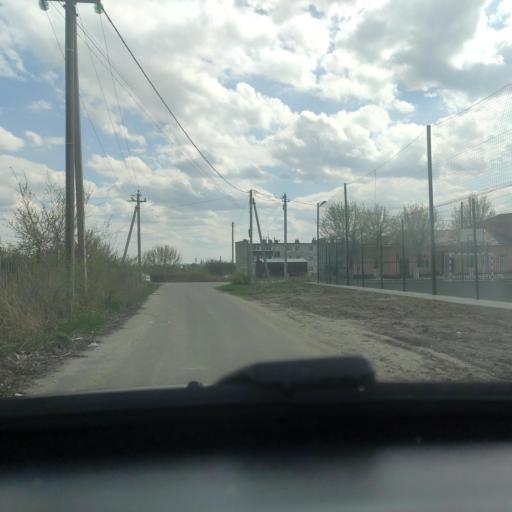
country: RU
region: Voronezj
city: Somovo
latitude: 51.6941
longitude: 39.3685
